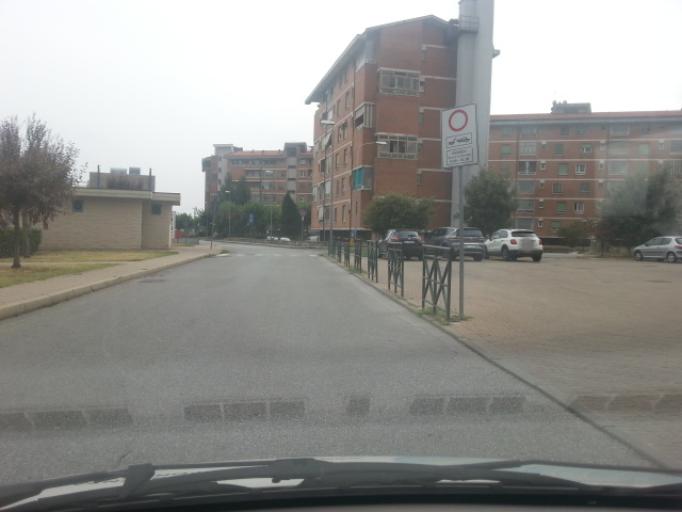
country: IT
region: Piedmont
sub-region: Provincia di Torino
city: Piossasco
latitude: 44.9896
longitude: 7.4767
